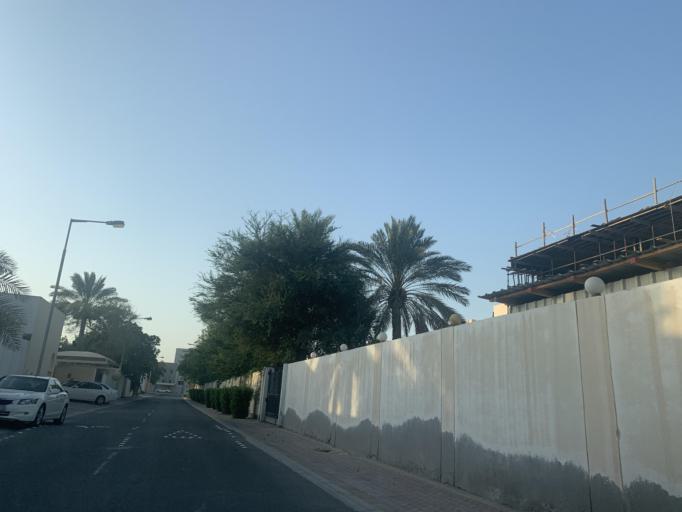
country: BH
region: Manama
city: Jidd Hafs
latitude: 26.2007
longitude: 50.5251
